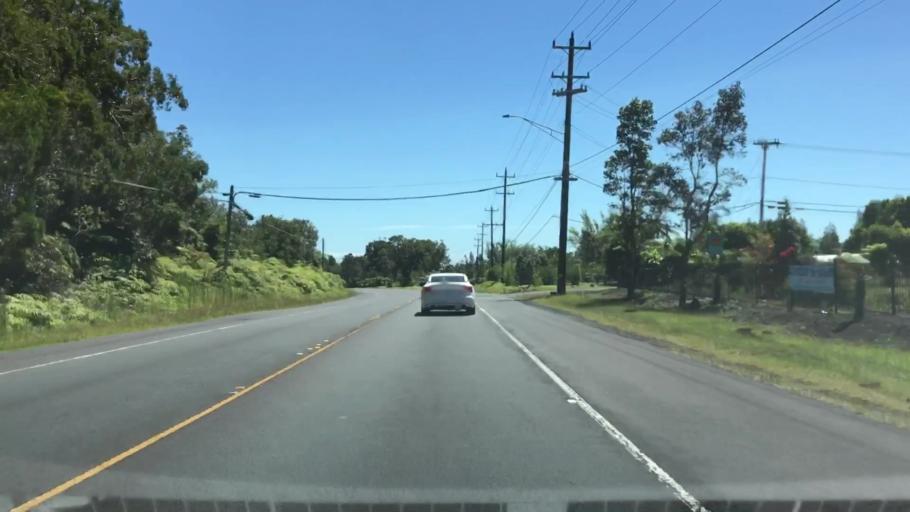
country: US
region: Hawaii
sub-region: Hawaii County
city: Volcano
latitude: 19.4544
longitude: -155.1764
